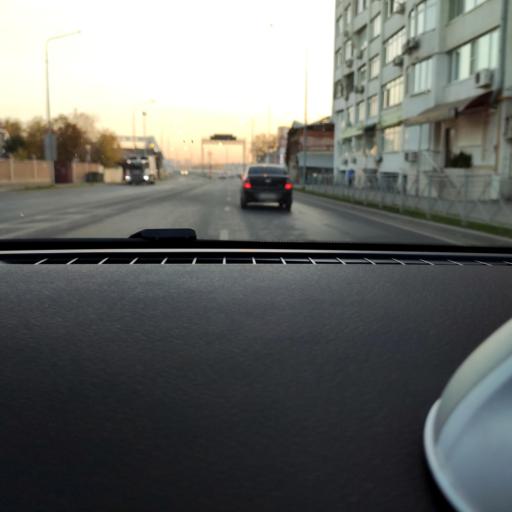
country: RU
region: Samara
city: Rozhdestveno
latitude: 53.1801
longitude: 50.0865
